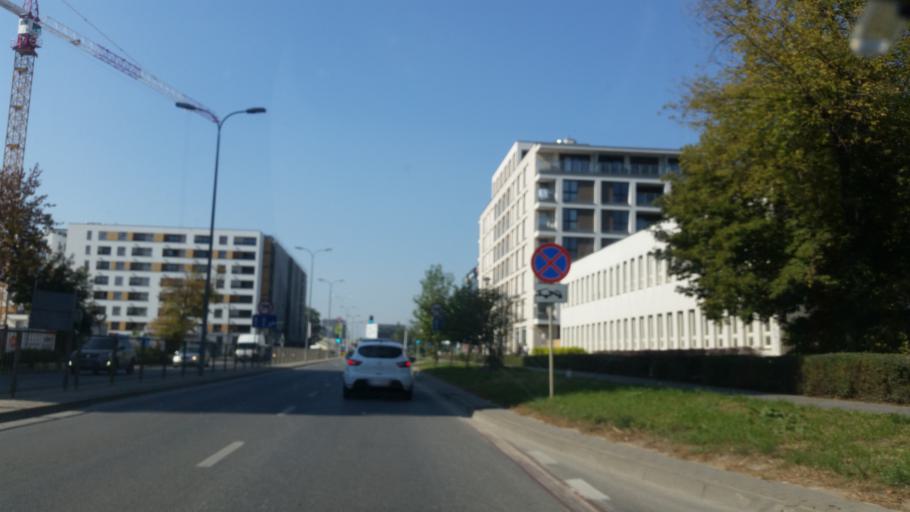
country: PL
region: Masovian Voivodeship
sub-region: Warszawa
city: Mokotow
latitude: 52.1762
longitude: 20.9941
